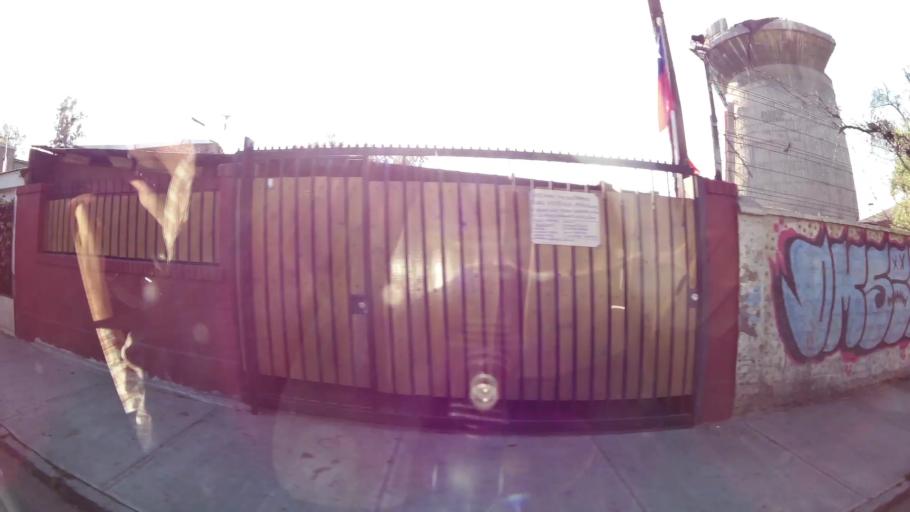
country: CL
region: Santiago Metropolitan
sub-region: Provincia de Santiago
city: Santiago
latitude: -33.3927
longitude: -70.6698
